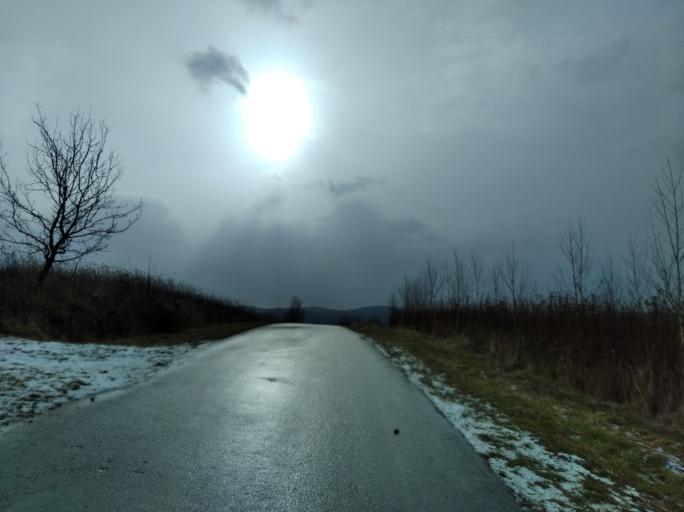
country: PL
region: Subcarpathian Voivodeship
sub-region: Powiat strzyzowski
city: Wysoka Strzyzowska
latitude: 49.8838
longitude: 21.7276
